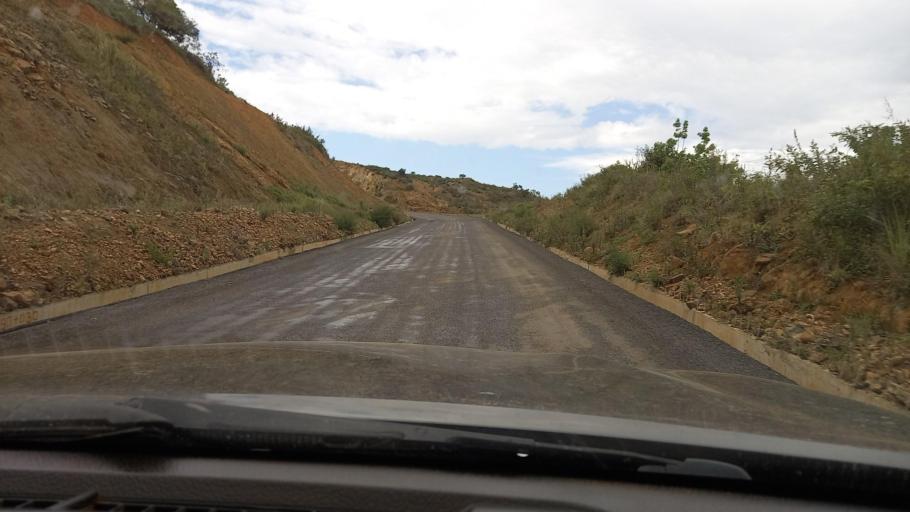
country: ET
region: Southern Nations, Nationalities, and People's Region
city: Mizan Teferi
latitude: 6.2122
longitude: 35.6565
